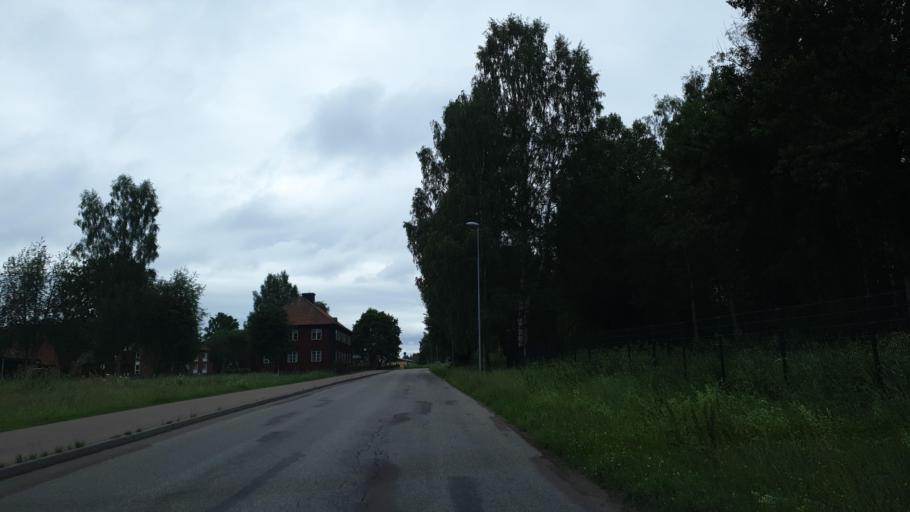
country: SE
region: Dalarna
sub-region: Mora Kommun
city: Mora
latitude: 60.9984
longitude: 14.5421
